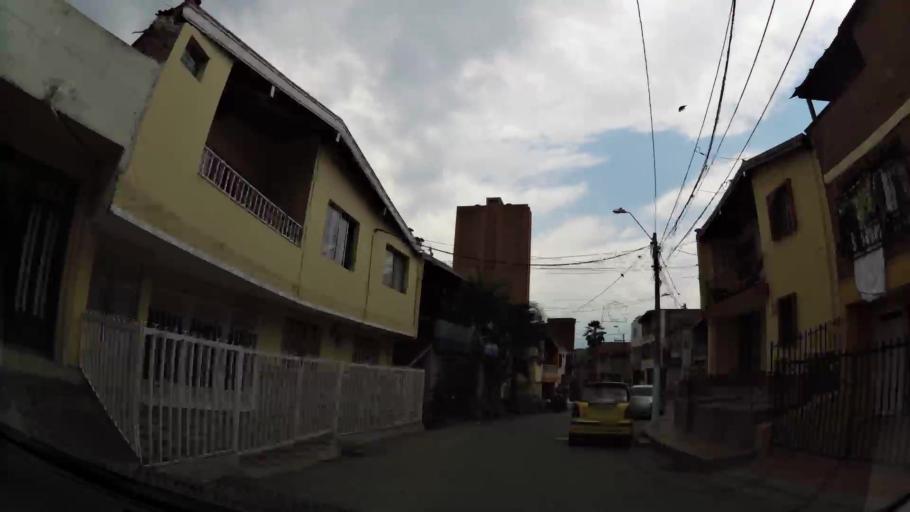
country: CO
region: Antioquia
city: Medellin
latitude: 6.2502
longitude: -75.5541
